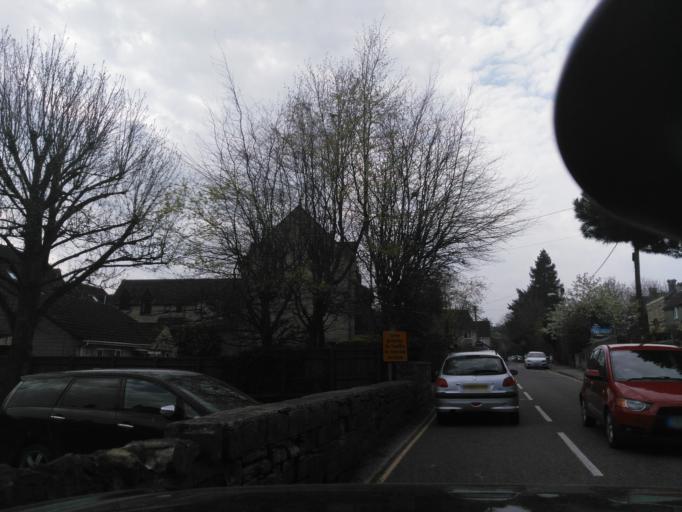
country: GB
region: England
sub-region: Wiltshire
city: Bradford-on-Avon
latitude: 51.3402
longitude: -2.2523
